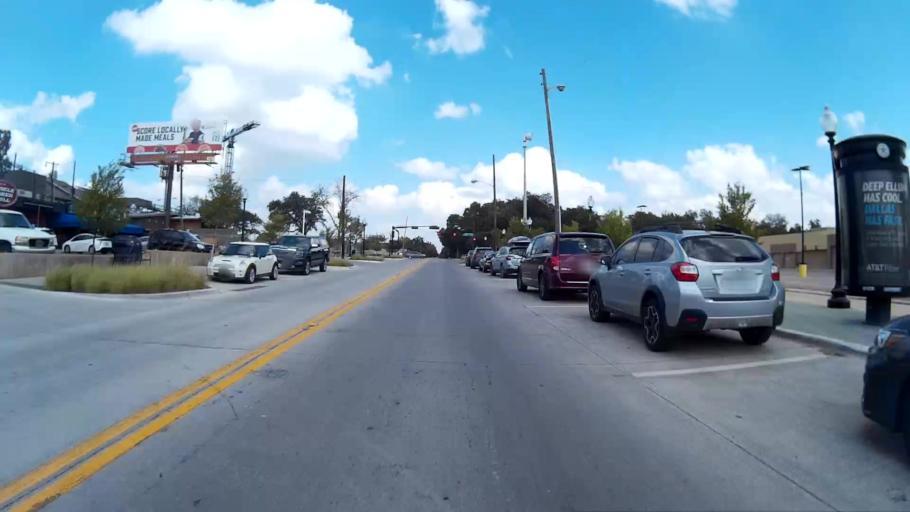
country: US
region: Texas
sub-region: Dallas County
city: Highland Park
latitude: 32.8164
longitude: -96.7702
